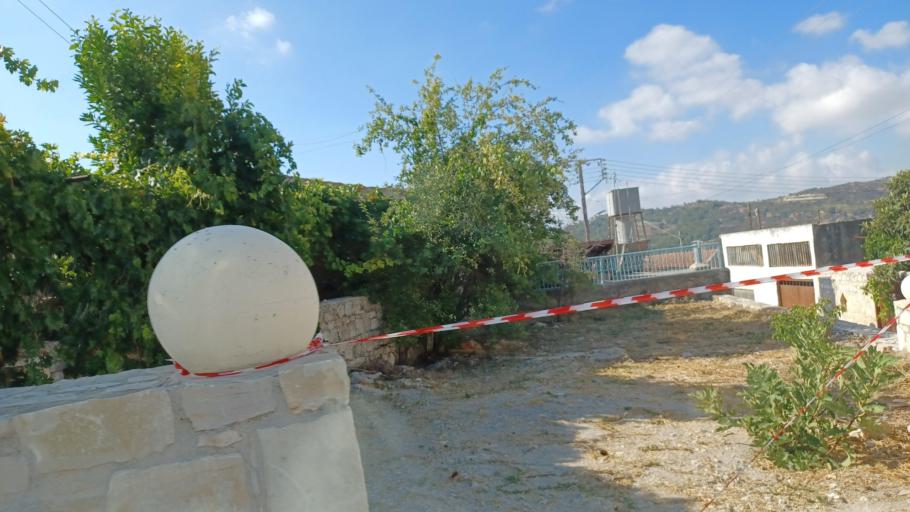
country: CY
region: Limassol
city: Pachna
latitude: 34.8490
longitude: 32.7066
